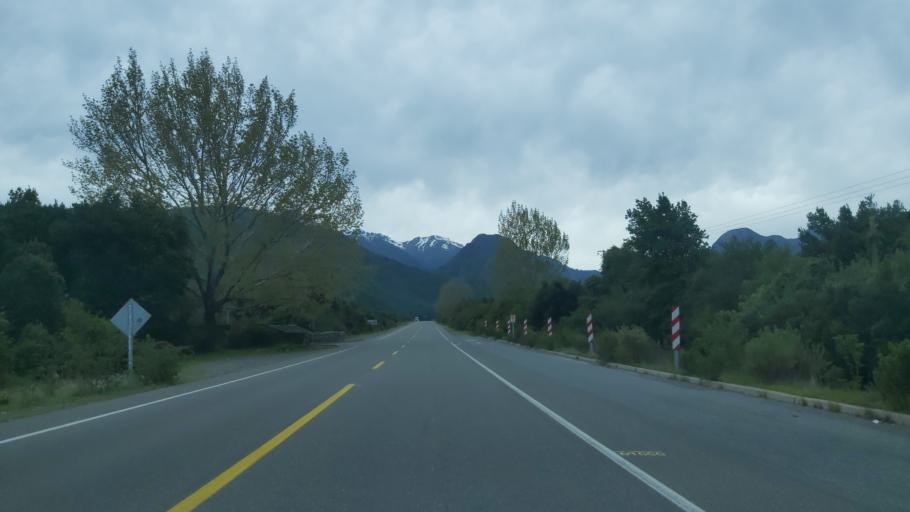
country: CL
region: Maule
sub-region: Provincia de Linares
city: Colbun
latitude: -35.7155
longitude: -71.1160
